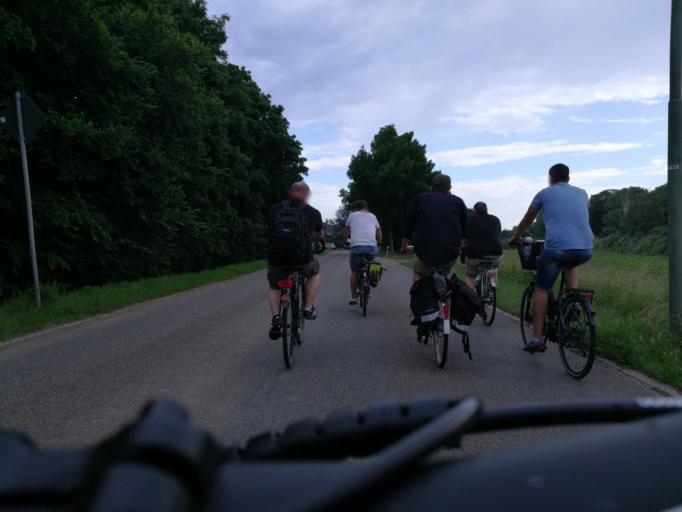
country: DE
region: North Rhine-Westphalia
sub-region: Regierungsbezirk Dusseldorf
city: Kleve
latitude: 51.8072
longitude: 6.1460
